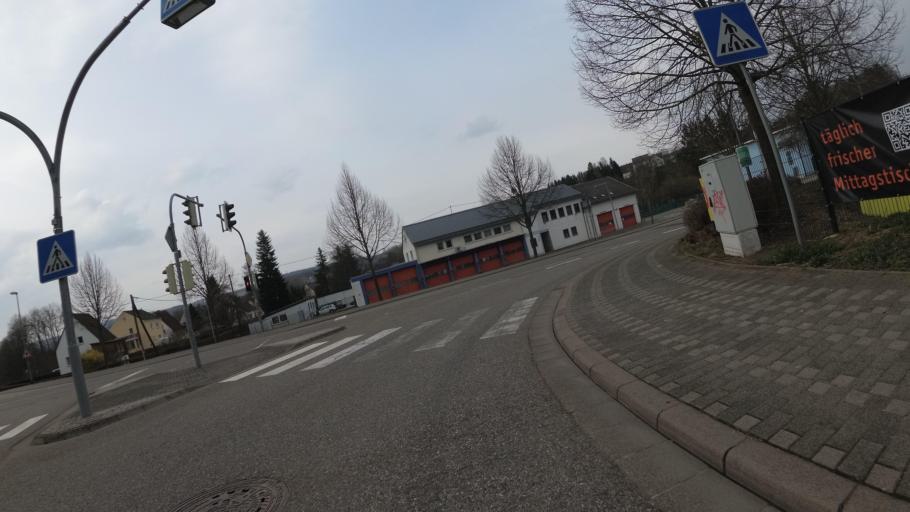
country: DE
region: Rheinland-Pfalz
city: Ellenberg
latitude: 49.6483
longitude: 7.1583
